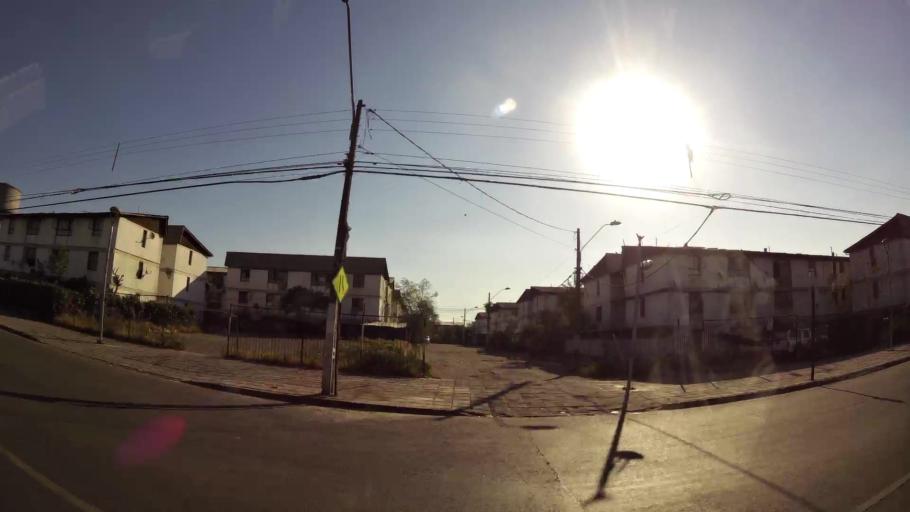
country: CL
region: Santiago Metropolitan
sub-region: Provincia de Santiago
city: La Pintana
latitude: -33.5506
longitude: -70.6293
